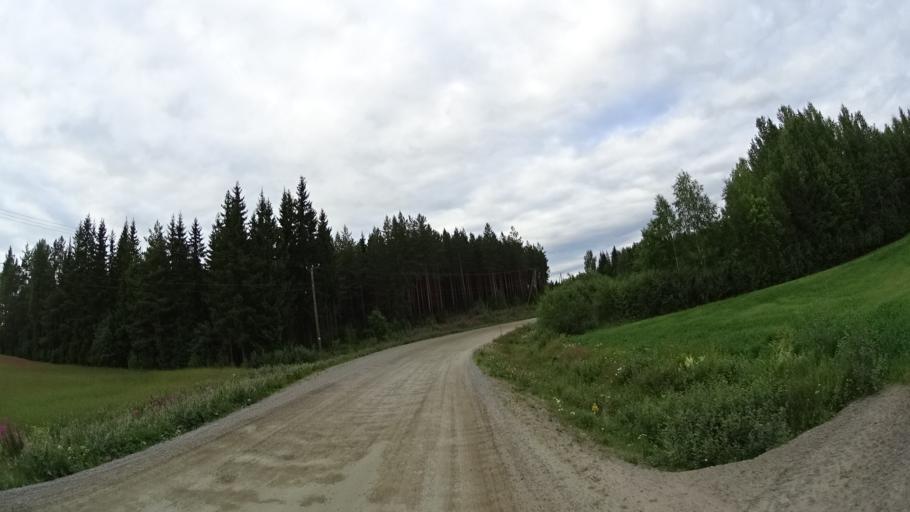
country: FI
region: Satakunta
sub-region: Pohjois-Satakunta
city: Jaemijaervi
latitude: 61.7732
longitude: 22.8596
